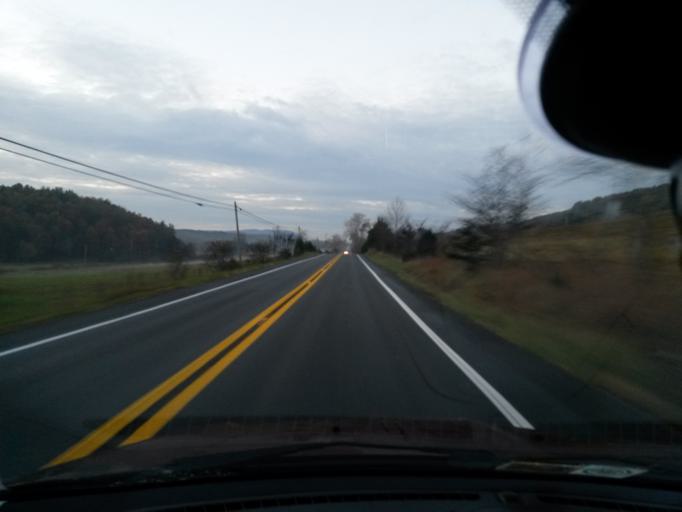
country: US
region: Virginia
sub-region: Alleghany County
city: Clifton Forge
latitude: 37.7332
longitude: -79.8004
